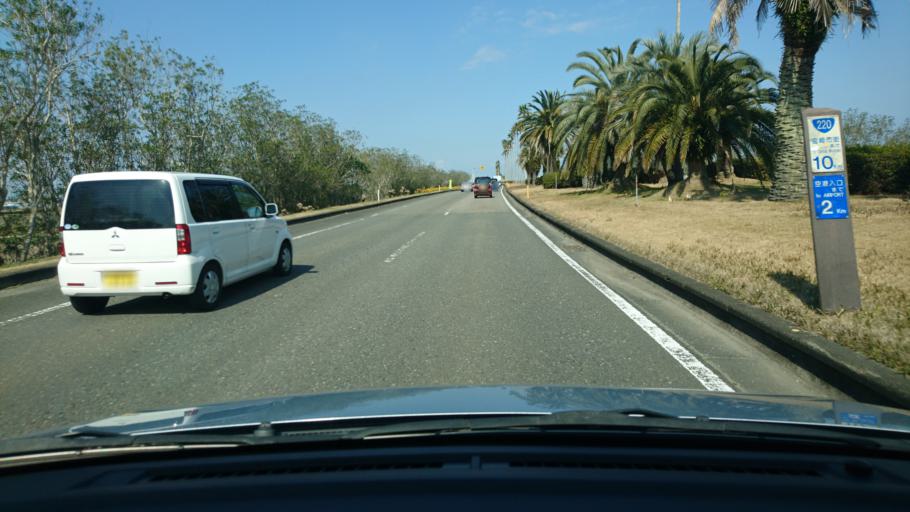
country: JP
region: Miyazaki
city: Miyazaki-shi
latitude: 31.8463
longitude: 131.4438
